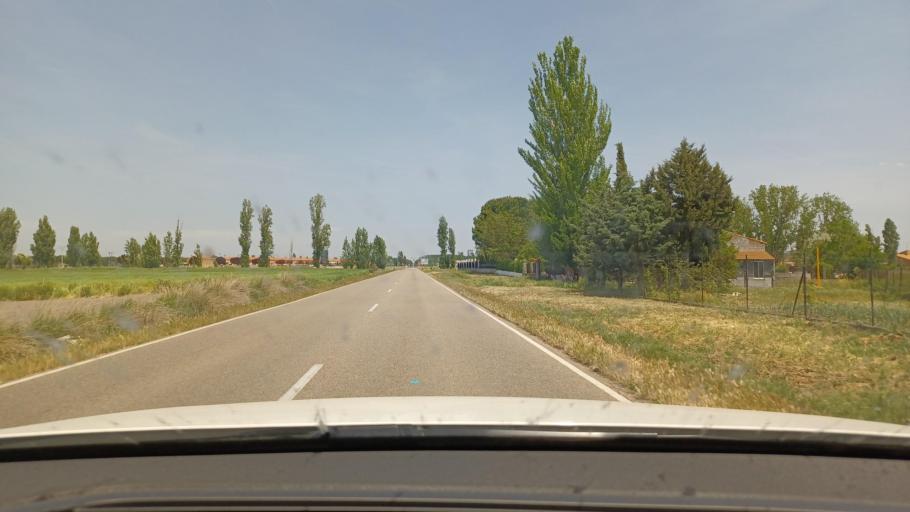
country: ES
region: Castille and Leon
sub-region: Provincia de Valladolid
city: Aldeamayor de San Martin
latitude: 41.5214
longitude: -4.6320
